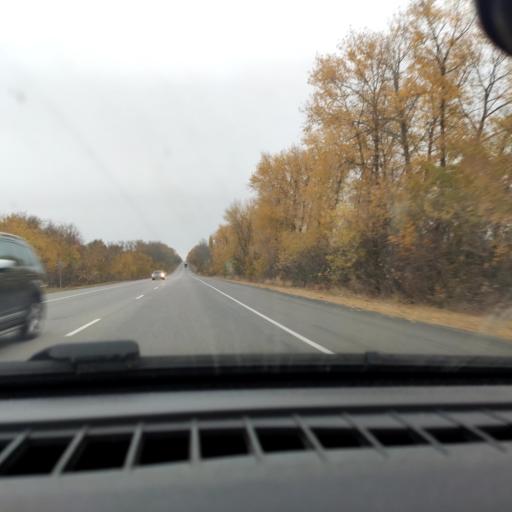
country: RU
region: Voronezj
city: Uryv-Pokrovka
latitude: 51.1537
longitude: 39.0637
